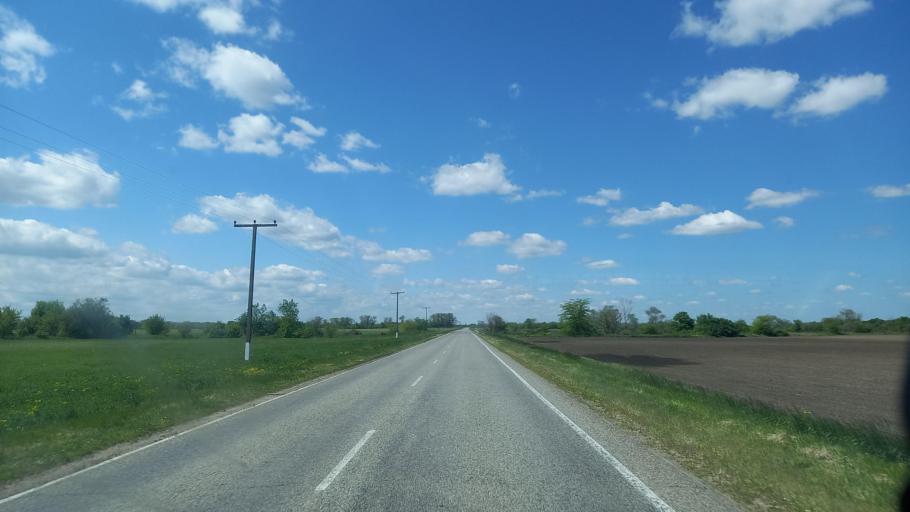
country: RU
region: Krasnodarskiy
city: Kazanskaya
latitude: 45.3516
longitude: 40.3489
